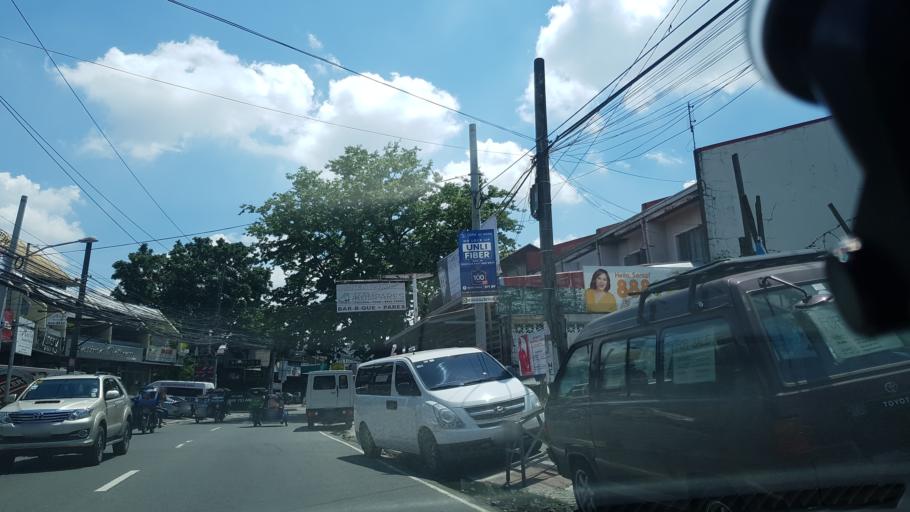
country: PH
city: Sambayanihan People's Village
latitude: 14.4558
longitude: 121.0310
